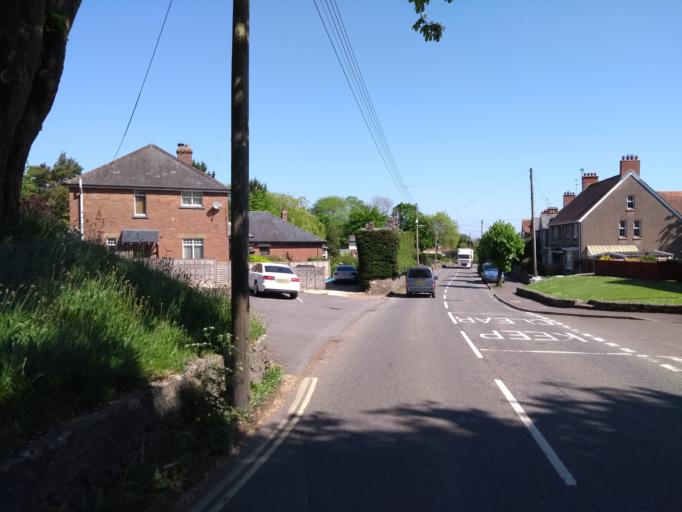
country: GB
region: England
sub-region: Somerset
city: Chard
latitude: 50.8743
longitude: -2.9599
